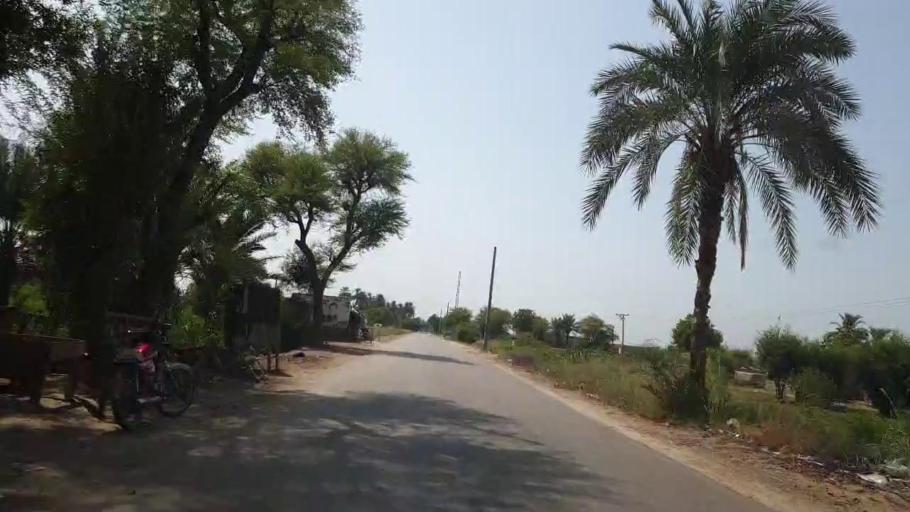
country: PK
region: Sindh
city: Bozdar
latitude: 27.1196
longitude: 68.5515
